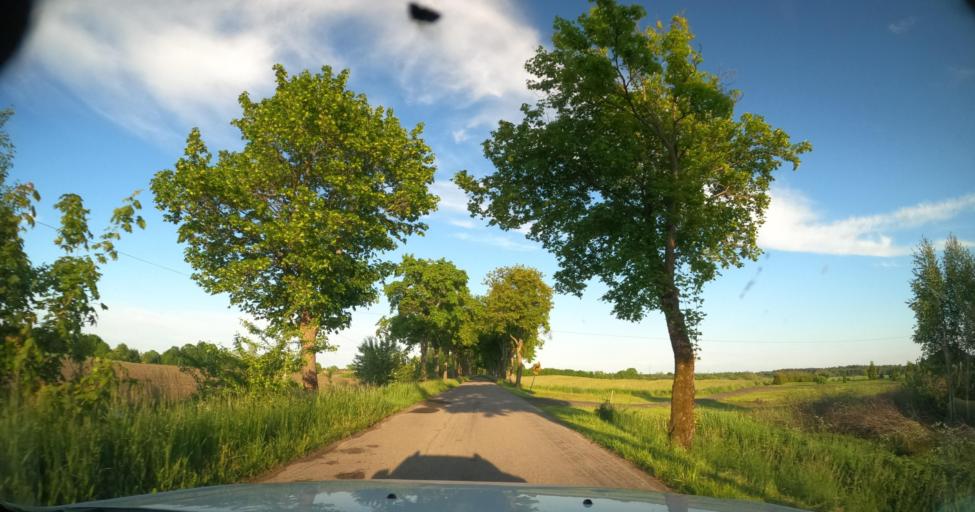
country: PL
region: Warmian-Masurian Voivodeship
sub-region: Powiat braniewski
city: Pieniezno
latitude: 54.1770
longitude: 20.1387
